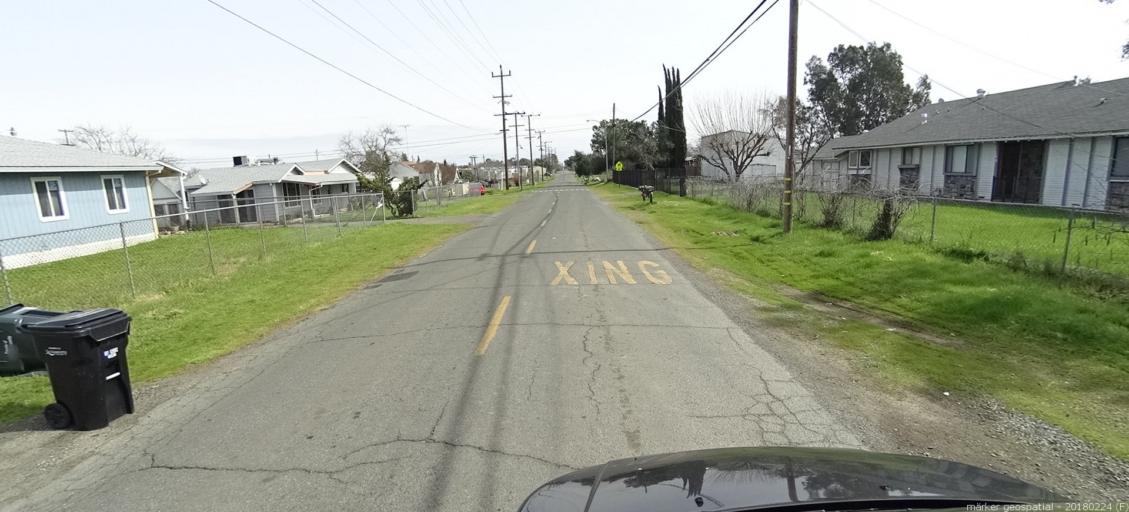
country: US
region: California
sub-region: Sacramento County
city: Elverta
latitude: 38.7100
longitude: -121.4647
